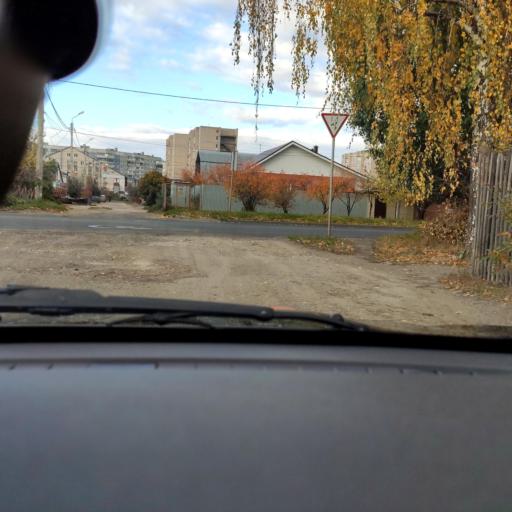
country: RU
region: Samara
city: Tol'yatti
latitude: 53.5363
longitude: 49.4005
